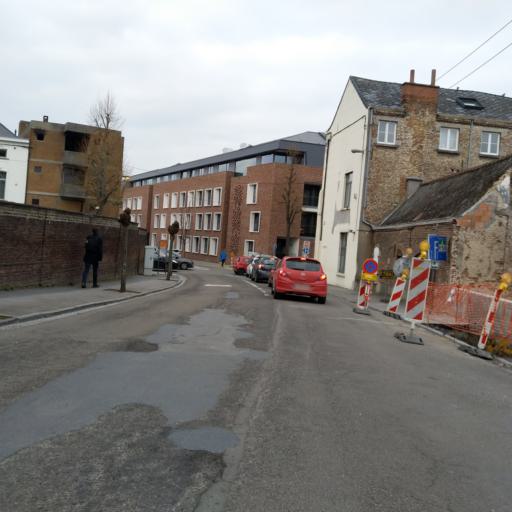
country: BE
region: Wallonia
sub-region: Province du Hainaut
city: Mons
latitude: 50.4592
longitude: 3.9543
